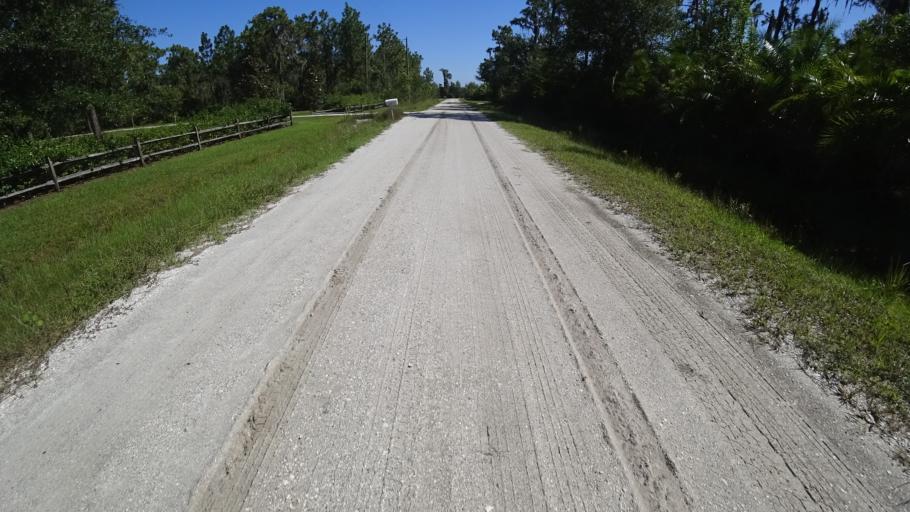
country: US
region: Florida
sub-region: Sarasota County
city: The Meadows
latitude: 27.4129
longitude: -82.2915
